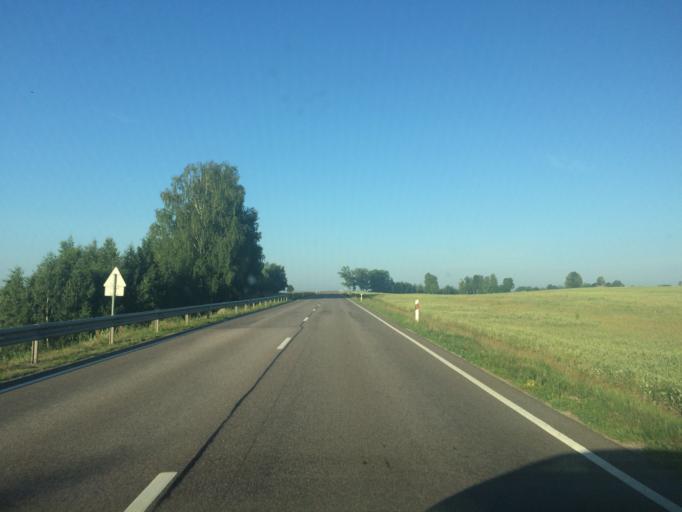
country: LT
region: Utenos apskritis
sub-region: Anyksciai
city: Anyksciai
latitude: 55.4063
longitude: 25.1907
